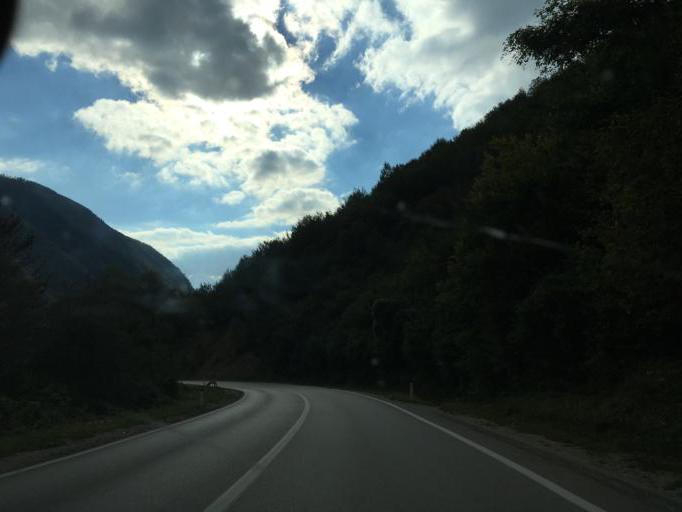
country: BA
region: Federation of Bosnia and Herzegovina
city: Bugojno
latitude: 44.0922
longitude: 17.5558
